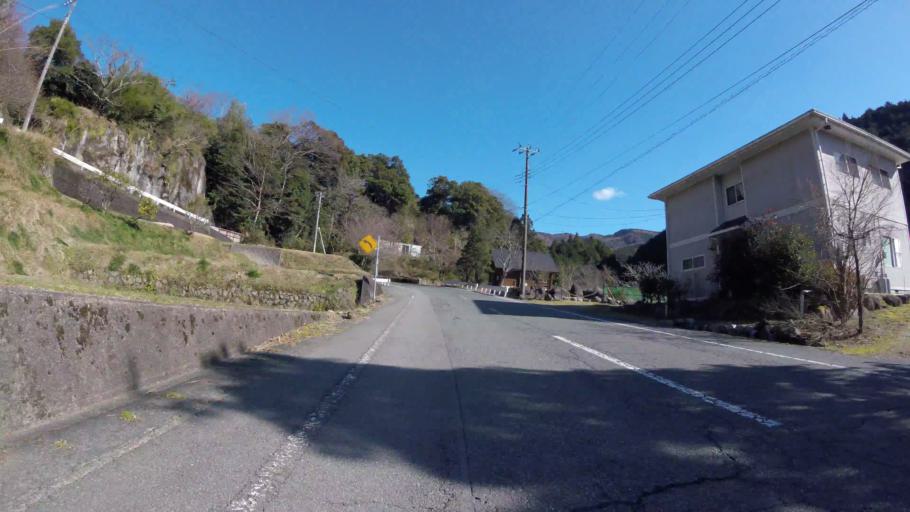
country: JP
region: Shizuoka
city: Ito
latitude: 34.8924
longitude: 138.9395
